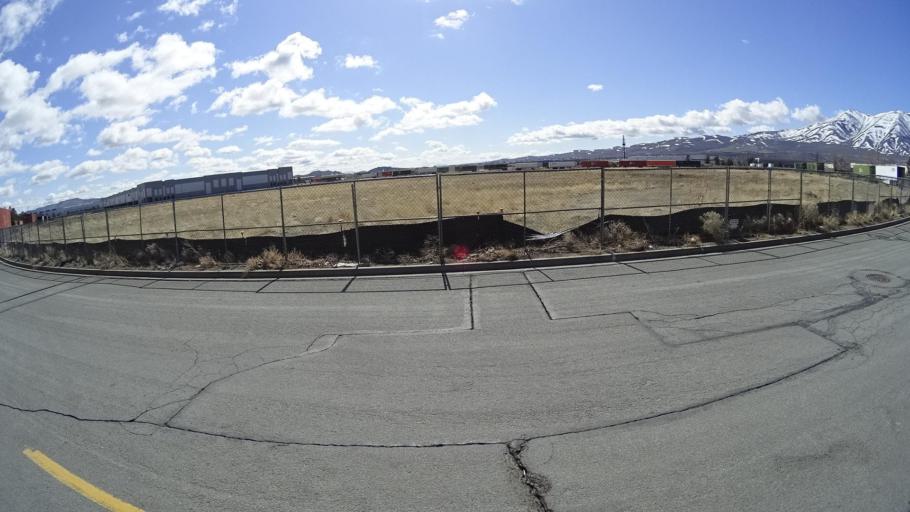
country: US
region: Nevada
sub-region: Washoe County
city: Lemmon Valley
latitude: 39.6570
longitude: -119.8964
